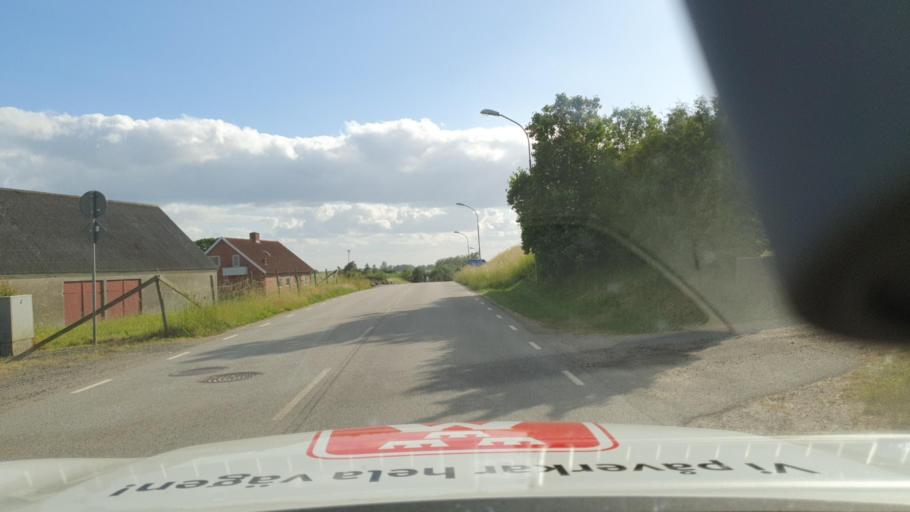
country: SE
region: Skane
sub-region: Tomelilla Kommun
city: Tomelilla
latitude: 55.5795
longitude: 14.0114
